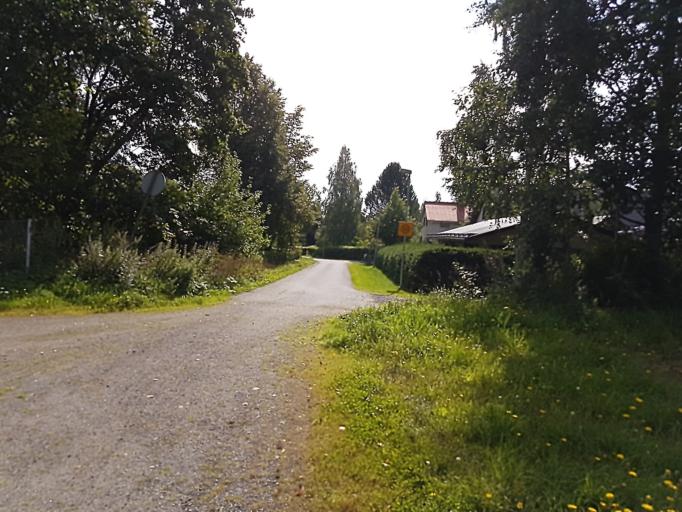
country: FI
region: Pirkanmaa
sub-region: Etelae-Pirkanmaa
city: Valkeakoski
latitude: 61.2527
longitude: 24.0414
